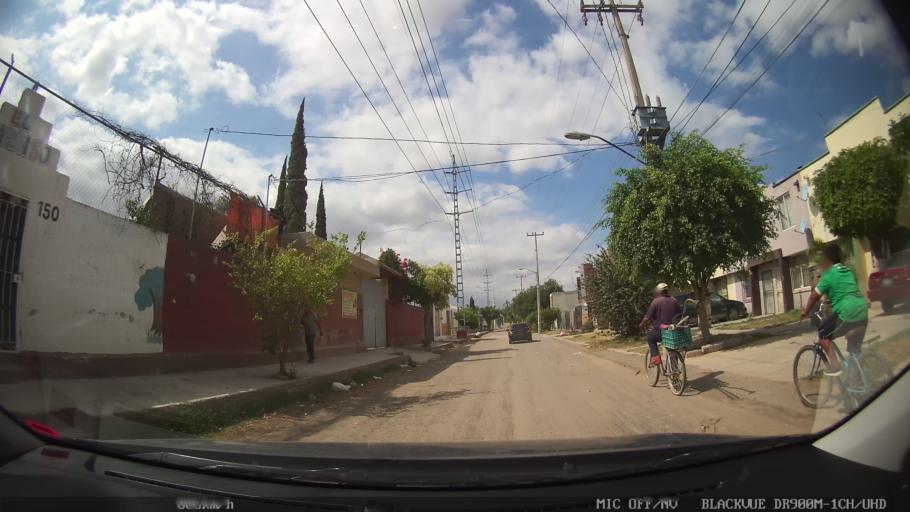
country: MX
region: Jalisco
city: Tonala
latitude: 20.6613
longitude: -103.2475
